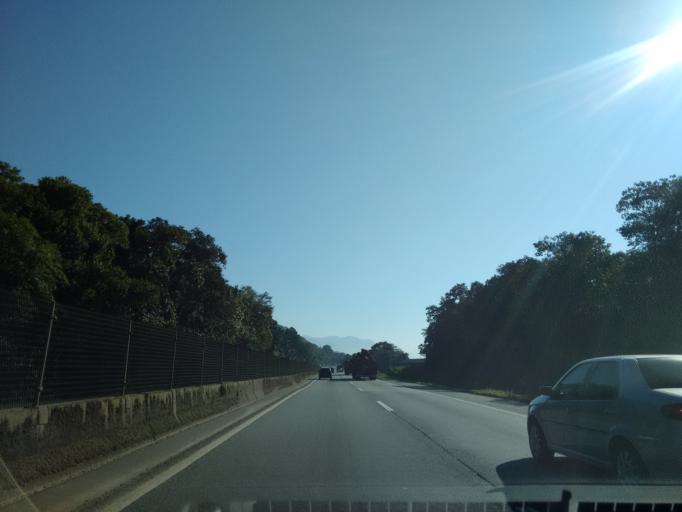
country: BR
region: Santa Catarina
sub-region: Joinville
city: Joinville
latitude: -26.2170
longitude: -48.9160
